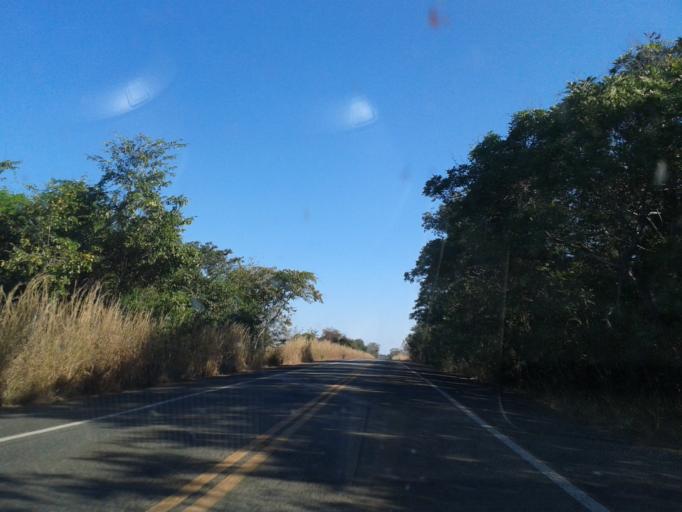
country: BR
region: Goias
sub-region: Mozarlandia
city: Mozarlandia
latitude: -15.0480
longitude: -50.6082
